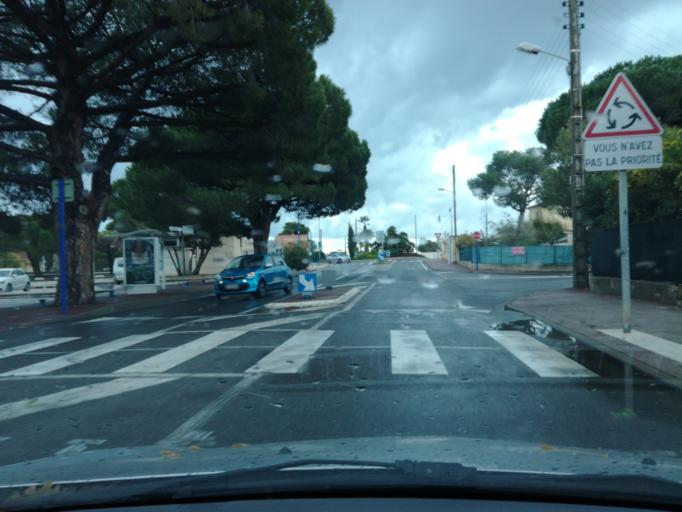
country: FR
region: Provence-Alpes-Cote d'Azur
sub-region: Departement du Var
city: Hyeres
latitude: 43.1063
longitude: 6.1753
